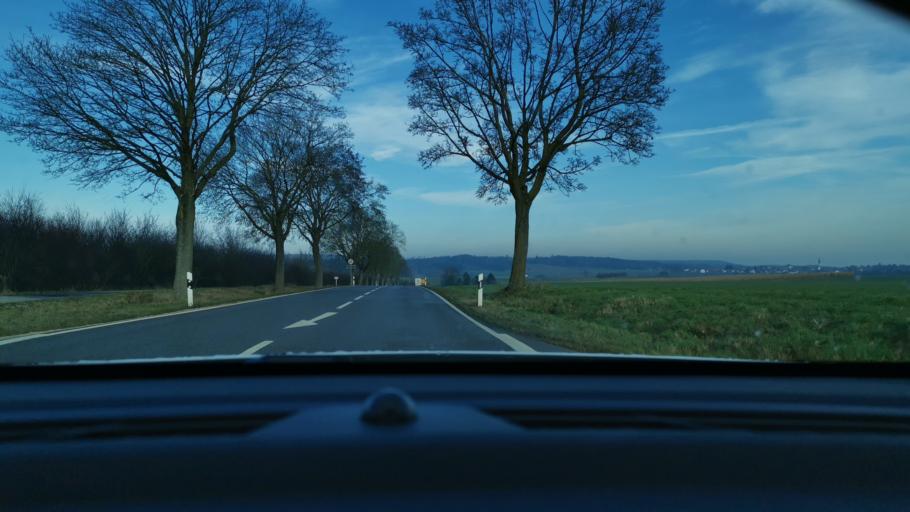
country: DE
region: Bavaria
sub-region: Swabia
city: Petersdorf
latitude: 48.5195
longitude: 11.0336
